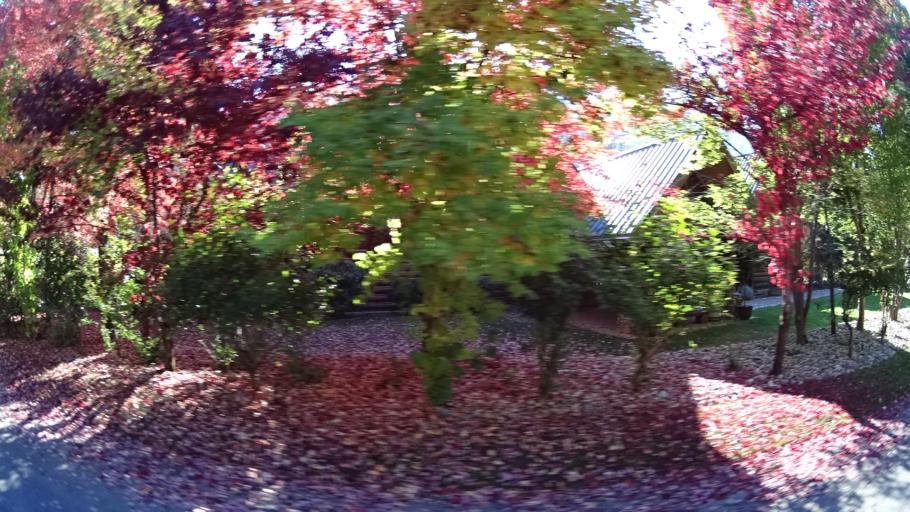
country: US
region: California
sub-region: Siskiyou County
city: Happy Camp
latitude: 41.6801
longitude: -123.1012
